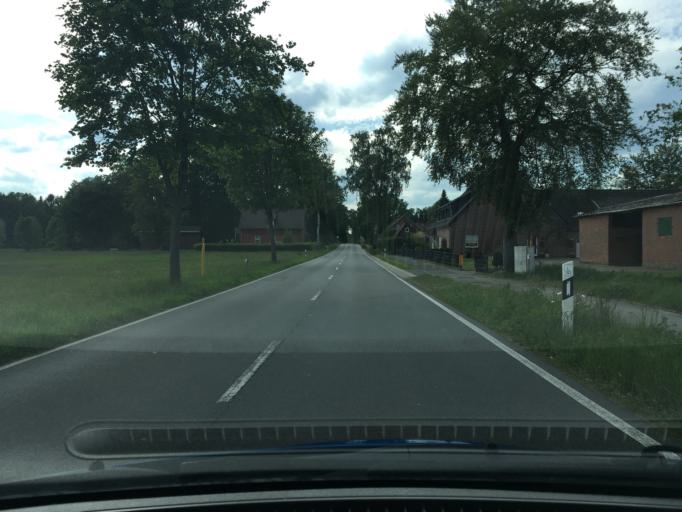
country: DE
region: Lower Saxony
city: Welle
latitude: 53.2453
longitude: 9.7937
